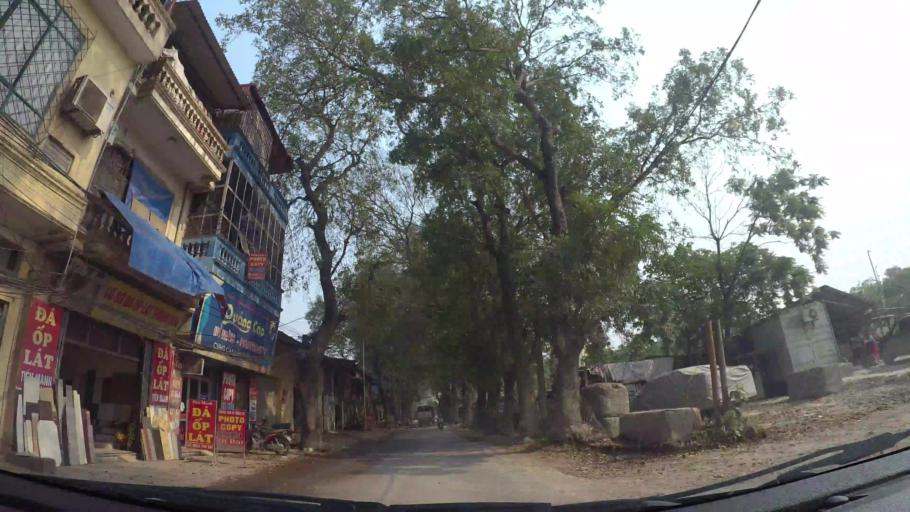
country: VN
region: Ha Noi
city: Ha Dong
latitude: 20.9968
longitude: 105.7523
